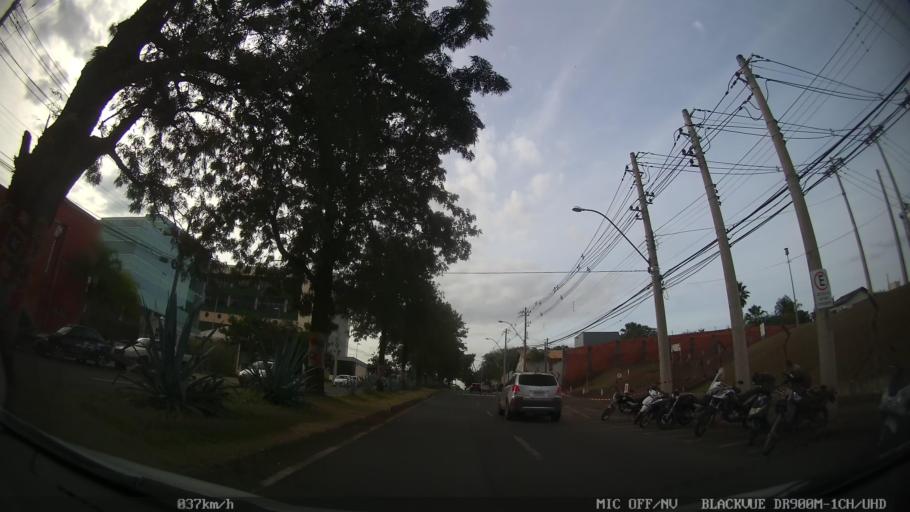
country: BR
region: Sao Paulo
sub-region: Piracicaba
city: Piracicaba
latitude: -22.7301
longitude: -47.6211
